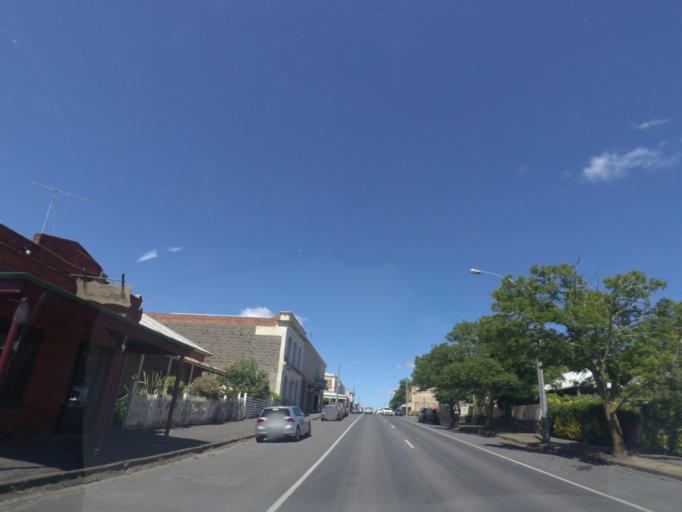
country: AU
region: Victoria
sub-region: Mount Alexander
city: Castlemaine
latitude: -37.2440
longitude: 144.4482
